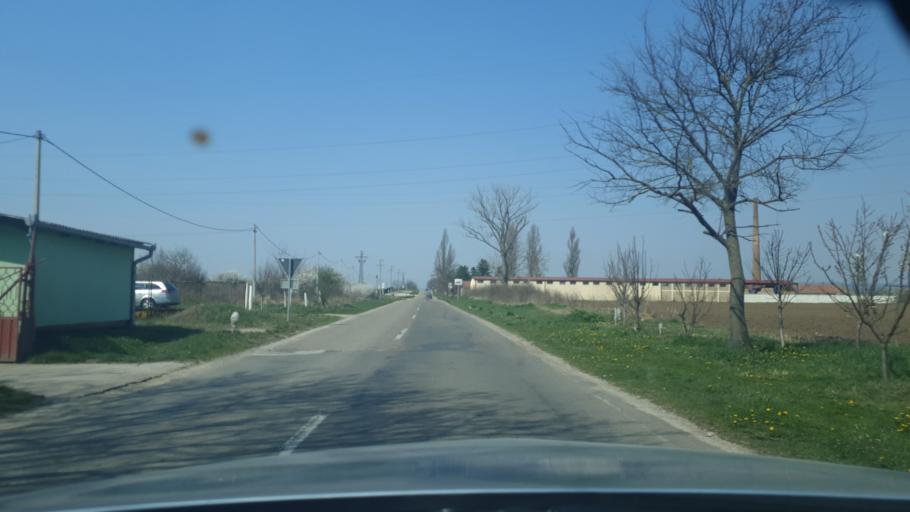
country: RS
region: Autonomna Pokrajina Vojvodina
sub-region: Sremski Okrug
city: Ruma
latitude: 45.0087
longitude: 19.7868
